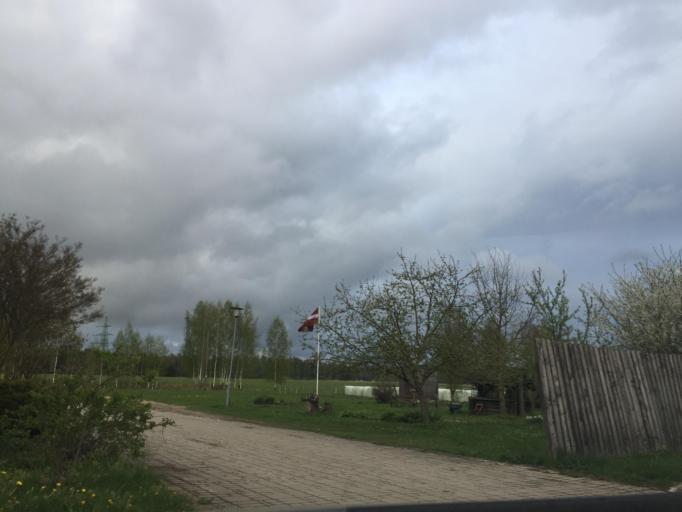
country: LV
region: Sigulda
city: Sigulda
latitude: 57.1537
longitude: 24.8991
